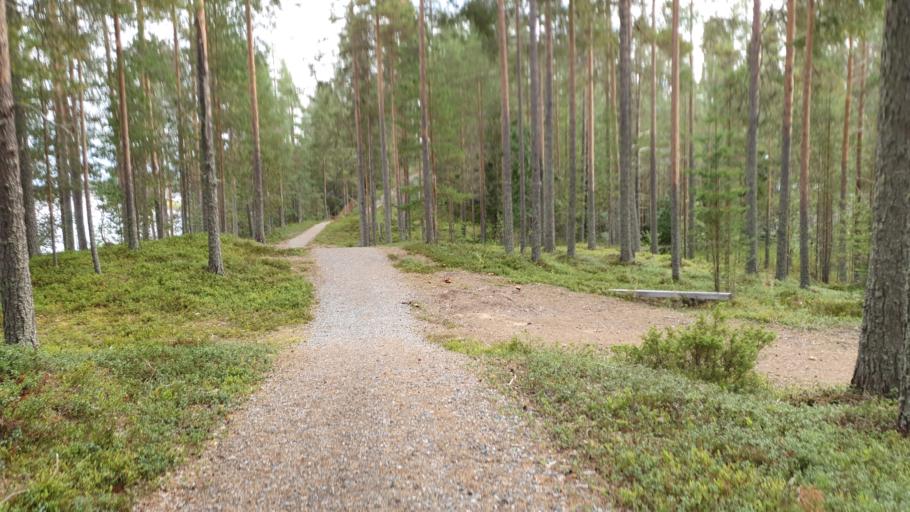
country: FI
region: Kainuu
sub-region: Kehys-Kainuu
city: Kuhmo
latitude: 64.1179
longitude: 29.5890
